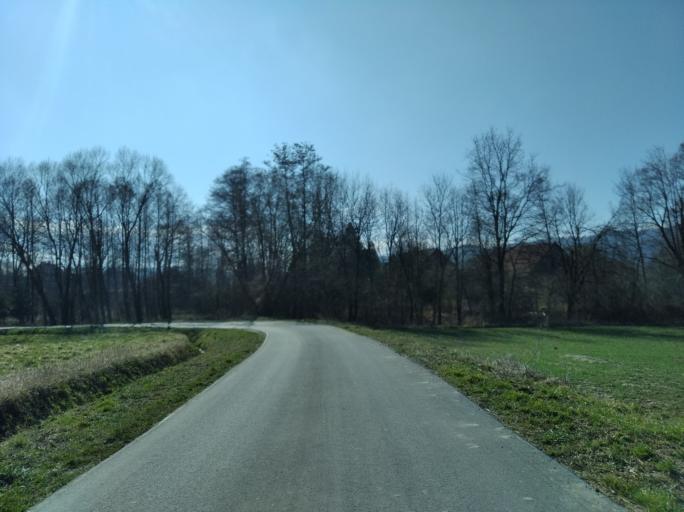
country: PL
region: Subcarpathian Voivodeship
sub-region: Powiat strzyzowski
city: Wysoka Strzyzowska
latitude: 49.8287
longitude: 21.7441
